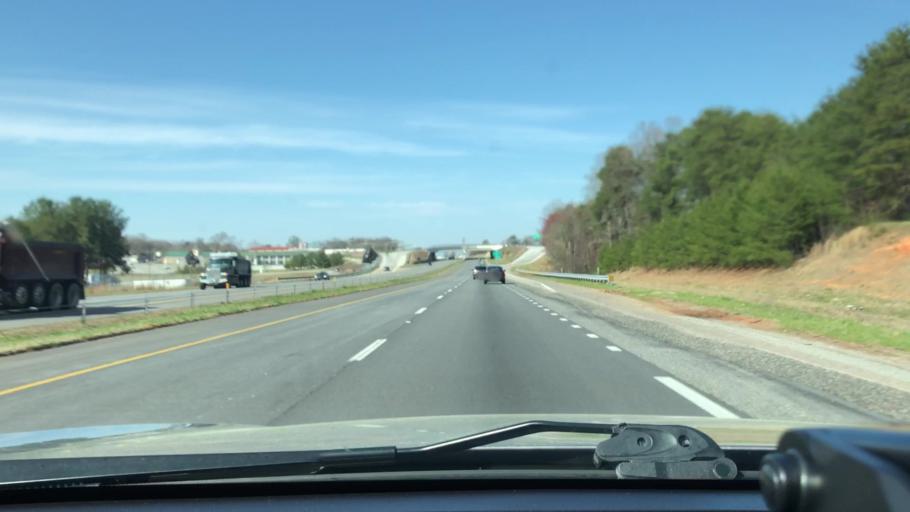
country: US
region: South Carolina
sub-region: Spartanburg County
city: Arcadia
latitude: 34.9161
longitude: -81.9895
